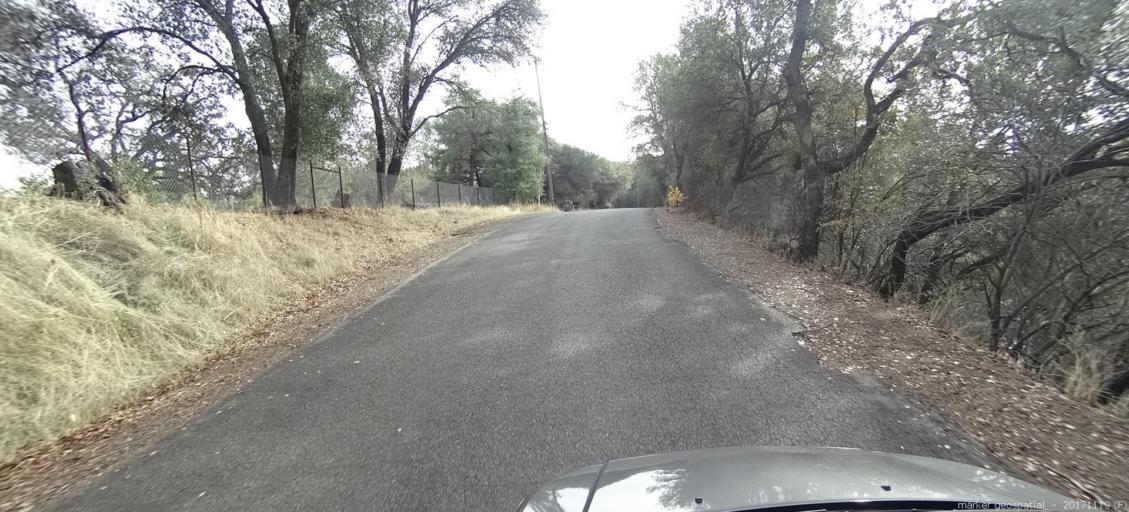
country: US
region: California
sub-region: Shasta County
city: Anderson
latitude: 40.4788
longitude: -122.3040
